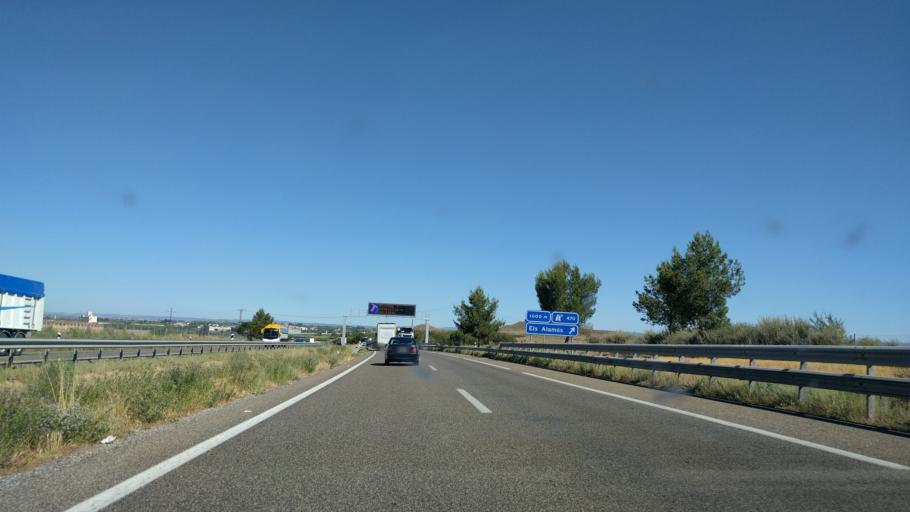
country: ES
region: Catalonia
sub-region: Provincia de Lleida
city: Alcoletge
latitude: 41.6323
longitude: 0.6940
